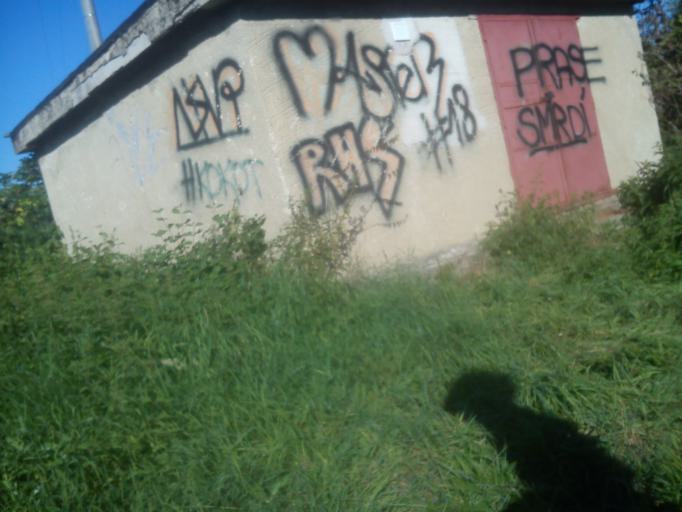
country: CZ
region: South Moravian
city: Sokolnice
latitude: 49.0997
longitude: 16.7569
